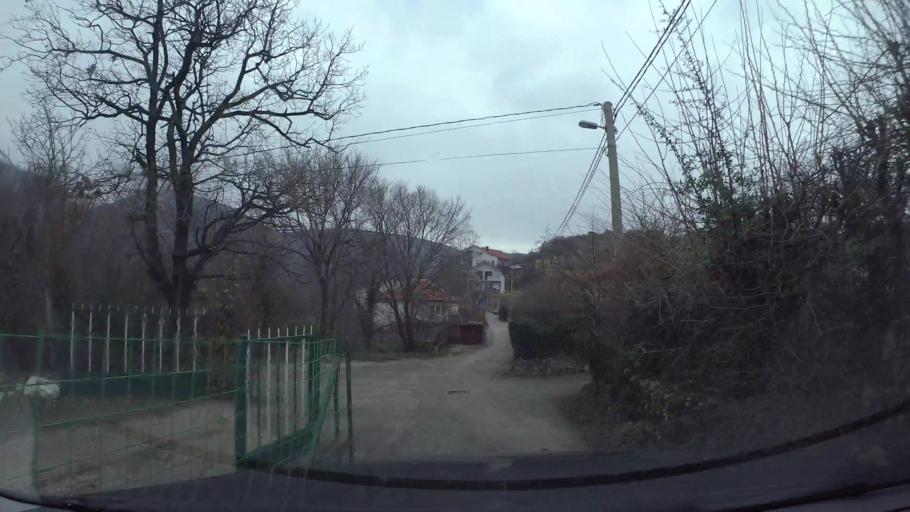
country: BA
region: Federation of Bosnia and Herzegovina
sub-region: Hercegovacko-Bosanski Kanton
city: Mostar
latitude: 43.3597
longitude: 17.8170
